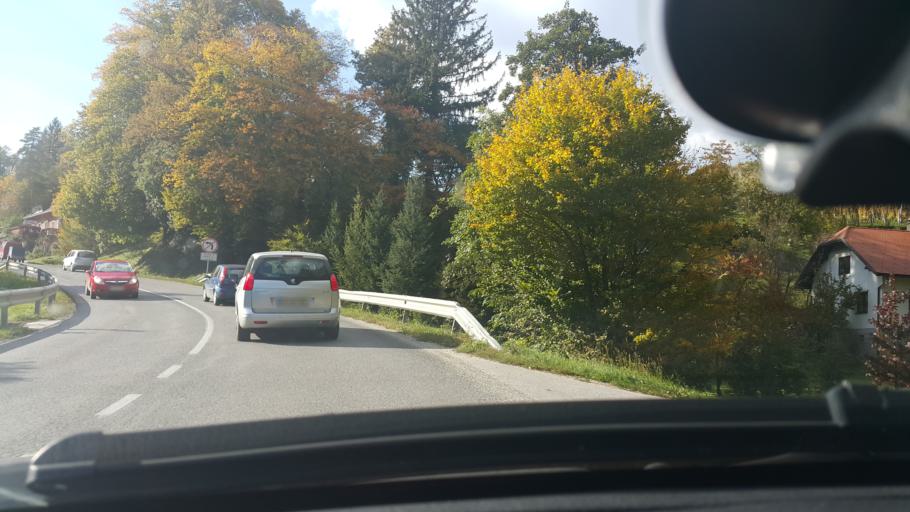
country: SI
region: Zrece
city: Zrece
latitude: 46.3589
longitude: 15.3762
